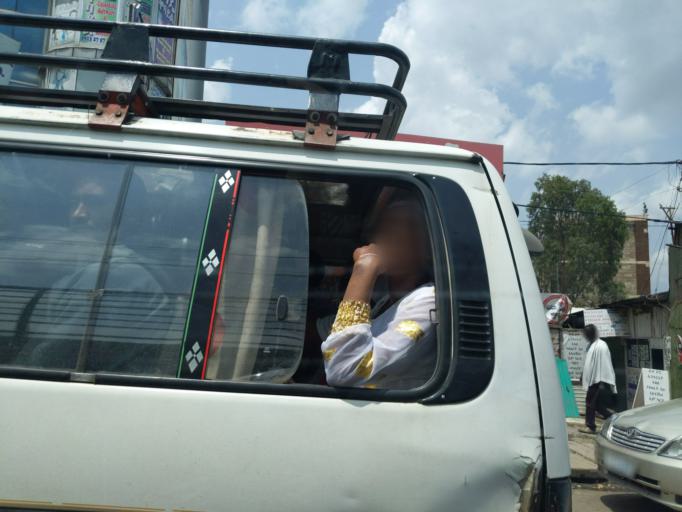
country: ET
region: Adis Abeba
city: Addis Ababa
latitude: 8.9567
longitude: 38.7639
